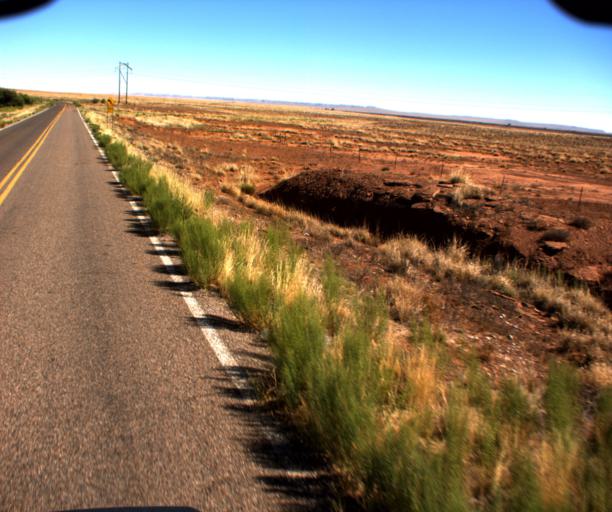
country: US
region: Arizona
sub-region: Coconino County
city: LeChee
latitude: 35.2522
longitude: -110.9615
